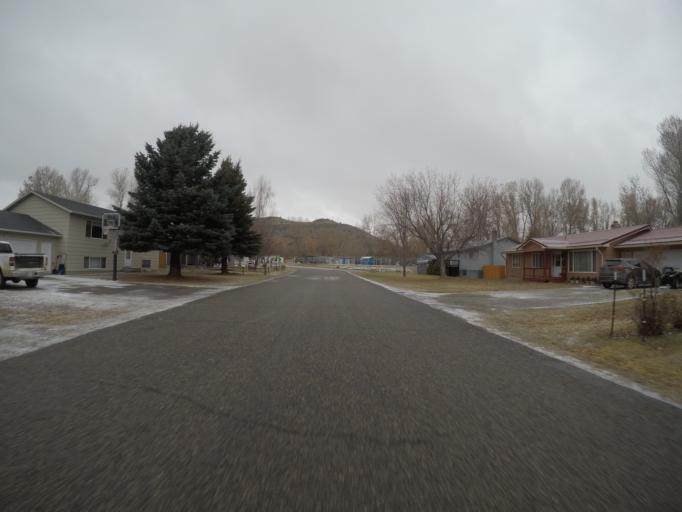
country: US
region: Montana
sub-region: Stillwater County
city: Absarokee
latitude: 45.5226
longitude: -109.4429
